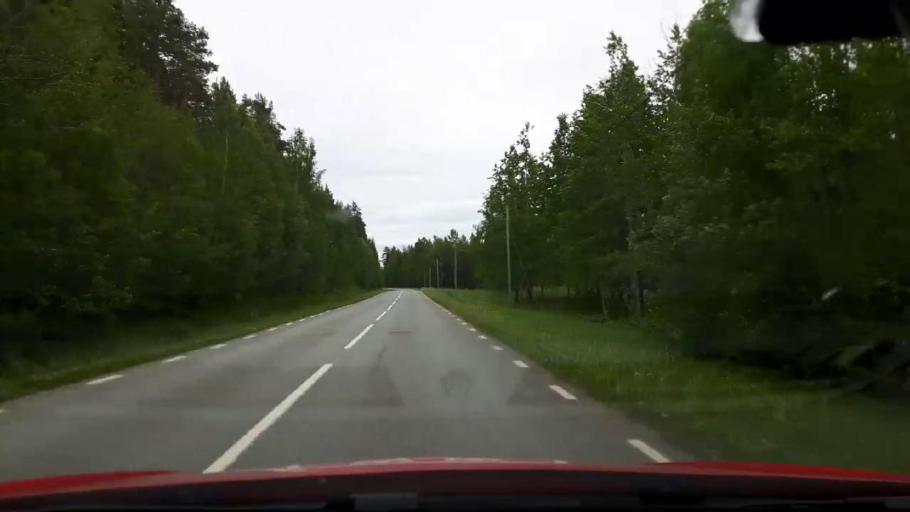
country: SE
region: Jaemtland
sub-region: Stroemsunds Kommun
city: Stroemsund
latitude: 63.4099
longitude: 15.6162
